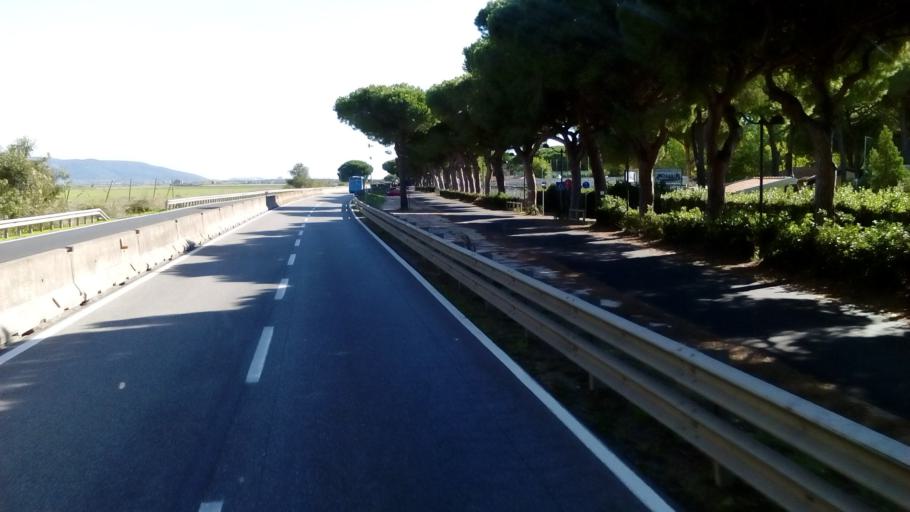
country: IT
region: Tuscany
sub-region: Provincia di Grosseto
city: Fonteblanda
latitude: 42.5357
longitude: 11.1843
